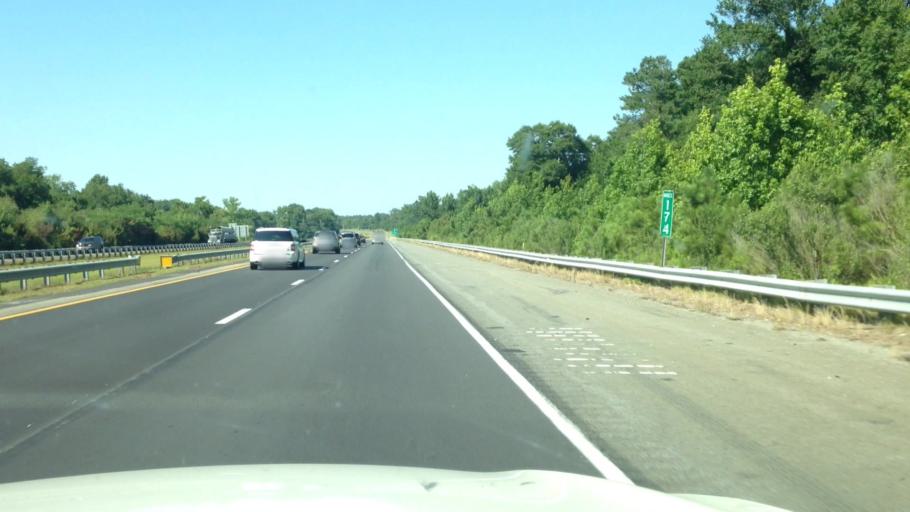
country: US
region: North Carolina
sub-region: Halifax County
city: Roanoke Rapids
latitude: 36.4465
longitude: -77.6236
